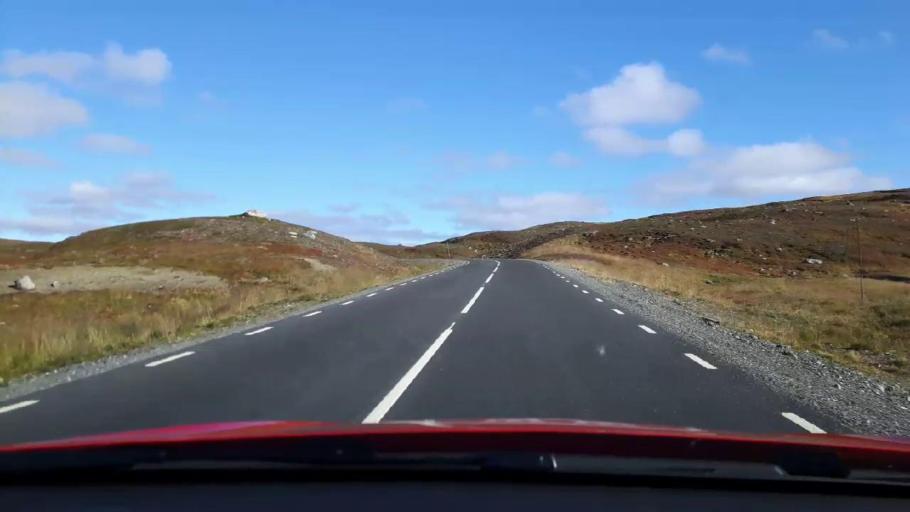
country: NO
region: Nordland
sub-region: Hattfjelldal
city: Hattfjelldal
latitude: 65.0493
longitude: 14.3406
